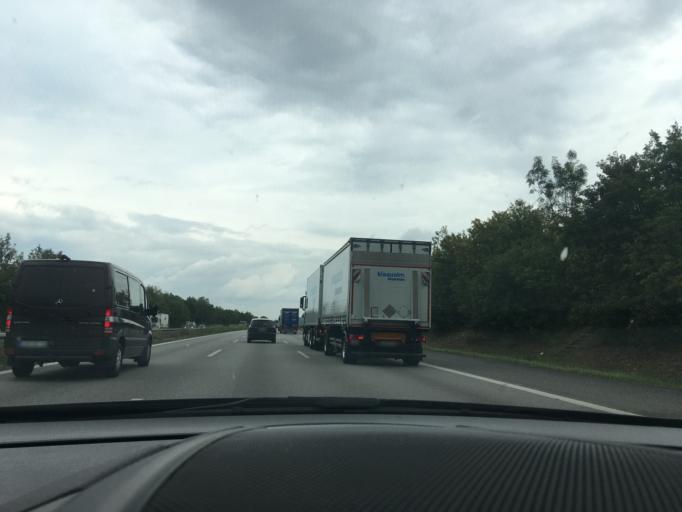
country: DE
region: Bavaria
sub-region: Upper Bavaria
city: Karlsfeld
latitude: 48.2158
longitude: 11.5045
